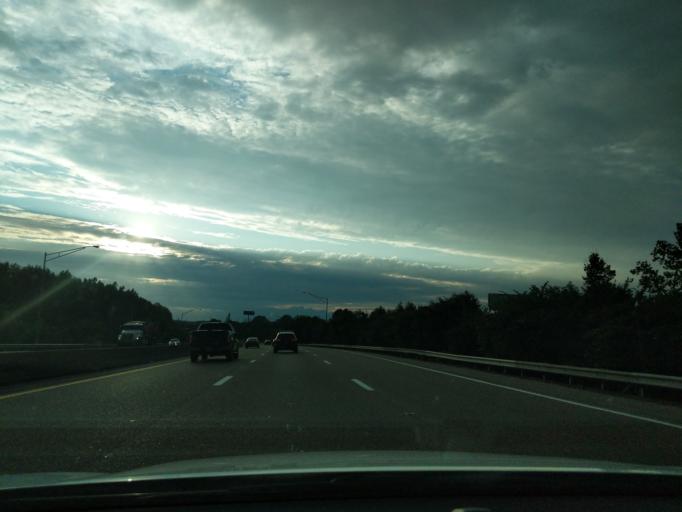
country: US
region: Tennessee
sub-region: Shelby County
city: New South Memphis
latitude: 35.0772
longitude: -90.0457
